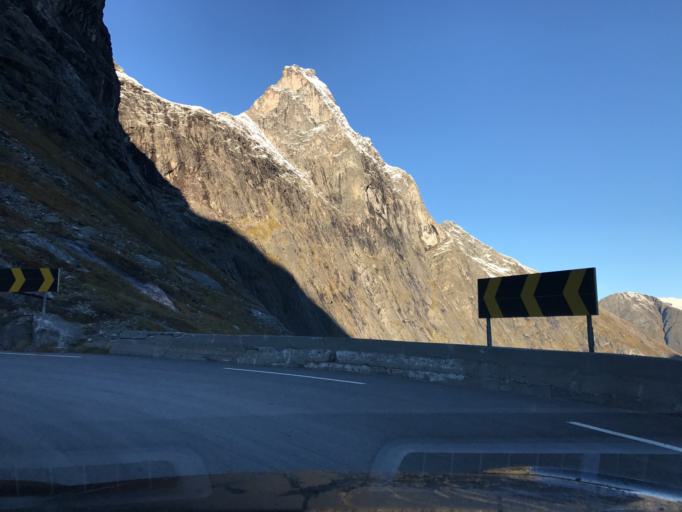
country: NO
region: More og Romsdal
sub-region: Rauma
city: Andalsnes
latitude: 62.4624
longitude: 7.6656
